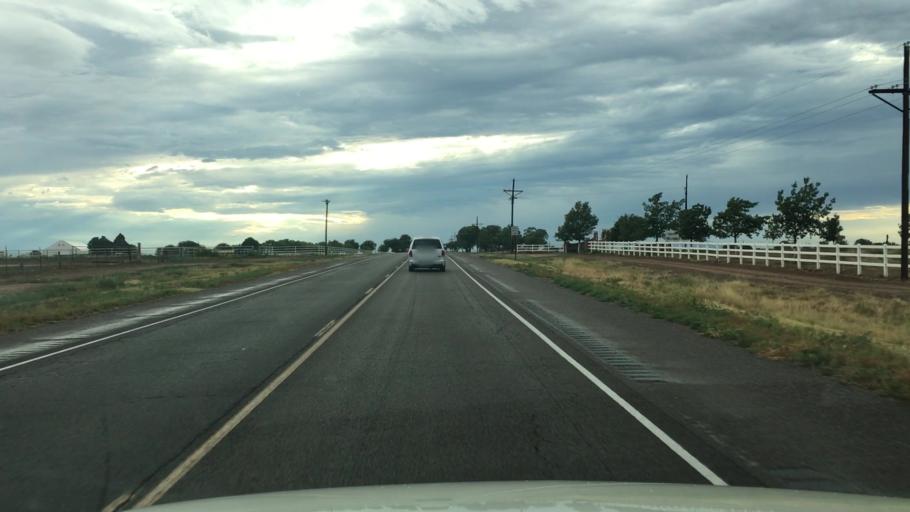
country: US
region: New Mexico
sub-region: Chaves County
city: Roswell
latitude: 33.3944
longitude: -104.4418
